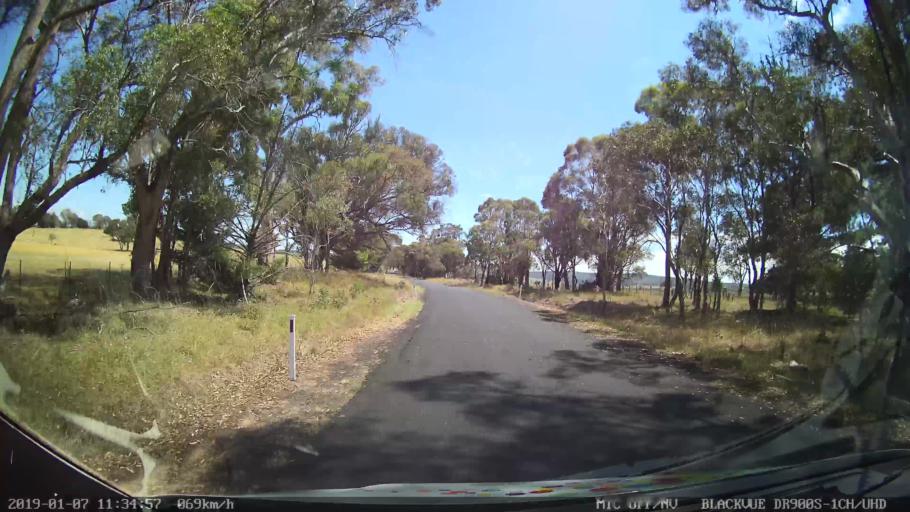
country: AU
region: New South Wales
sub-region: Armidale Dumaresq
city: Armidale
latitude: -30.3851
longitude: 151.5576
